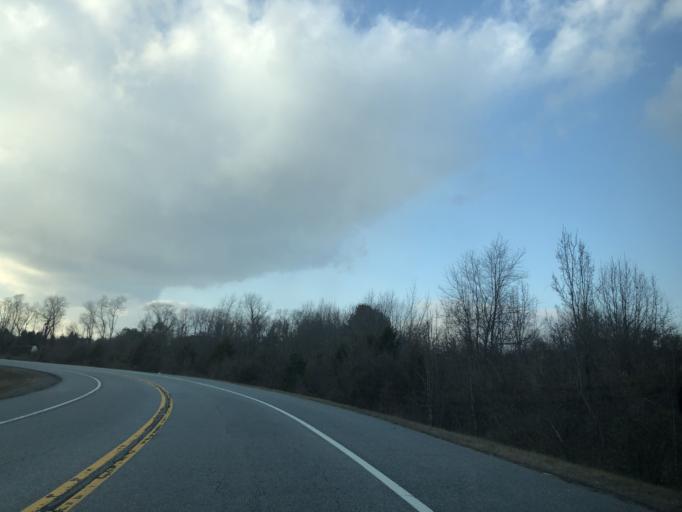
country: US
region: Delaware
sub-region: New Castle County
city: Bear
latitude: 39.6317
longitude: -75.6499
